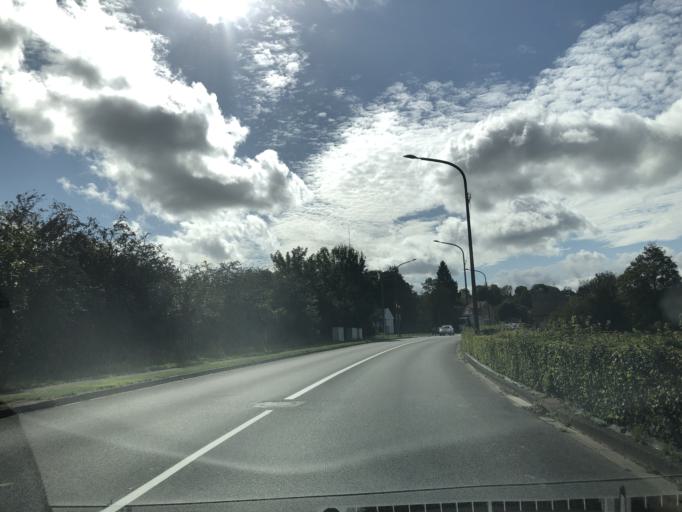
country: FR
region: Nord-Pas-de-Calais
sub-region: Departement du Pas-de-Calais
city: Hallines
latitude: 50.7077
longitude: 2.2301
